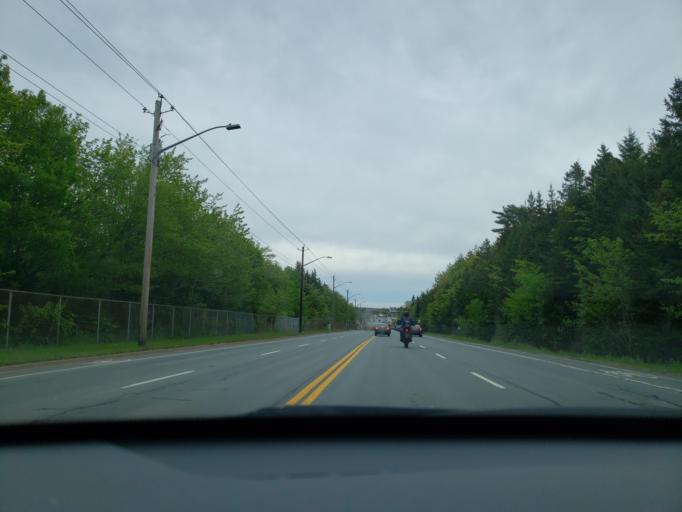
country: CA
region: Nova Scotia
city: Cole Harbour
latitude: 44.6905
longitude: -63.5078
